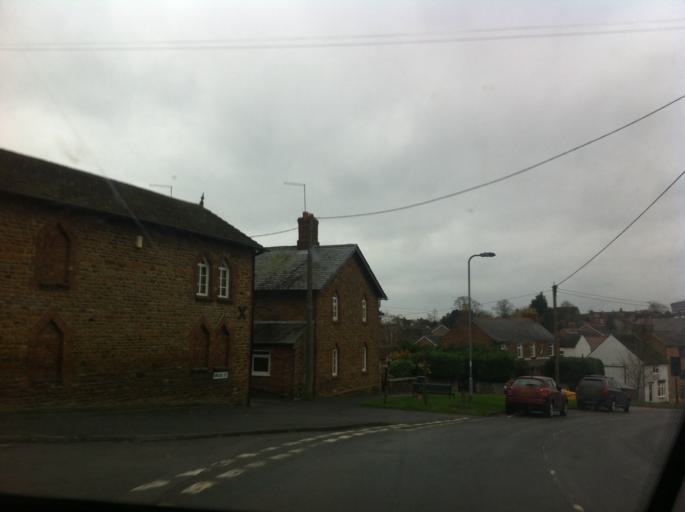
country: GB
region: England
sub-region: Northamptonshire
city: Wellingborough
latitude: 52.2613
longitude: -0.6949
